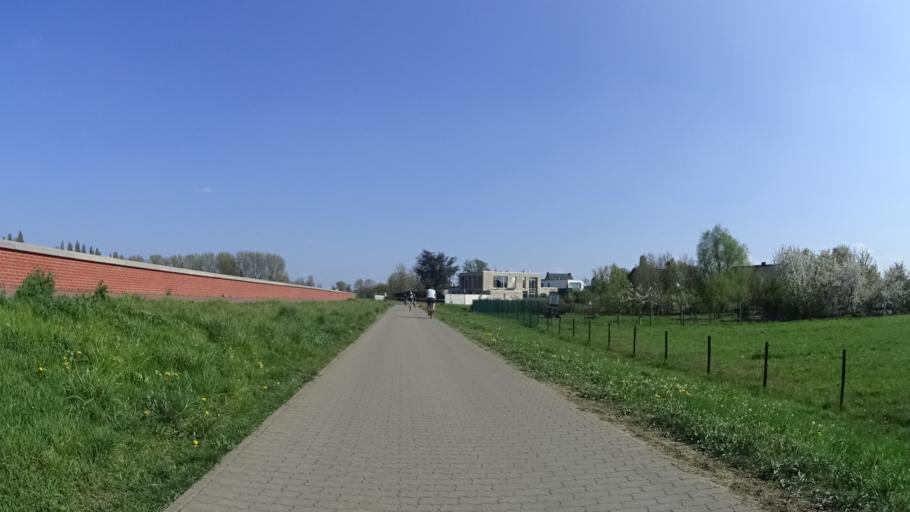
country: DE
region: North Rhine-Westphalia
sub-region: Regierungsbezirk Dusseldorf
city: Meerbusch
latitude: 51.2555
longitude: 6.7145
